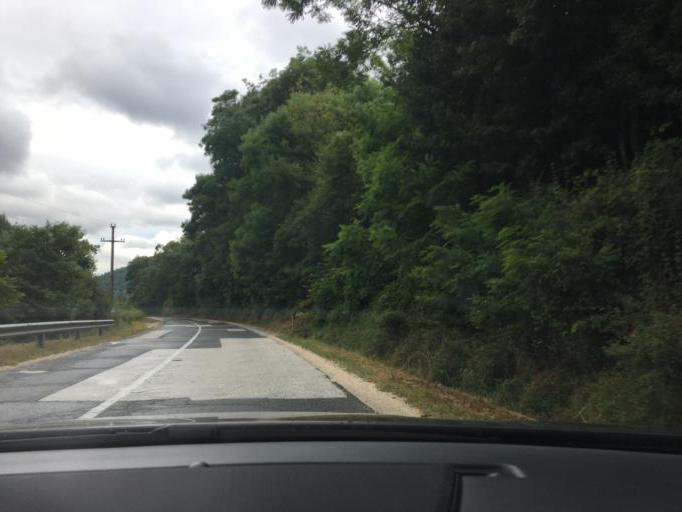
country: MK
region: Kriva Palanka
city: Kriva Palanka
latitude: 42.2243
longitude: 22.4191
